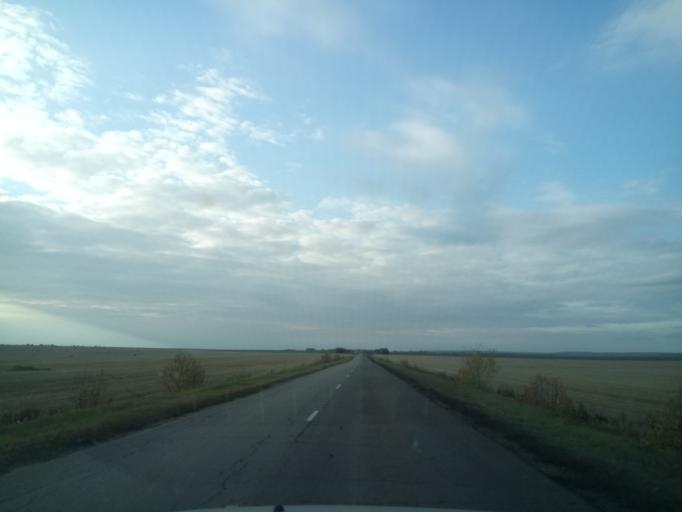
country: RU
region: Nizjnij Novgorod
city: Bol'shoye Boldino
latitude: 55.1388
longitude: 45.2349
